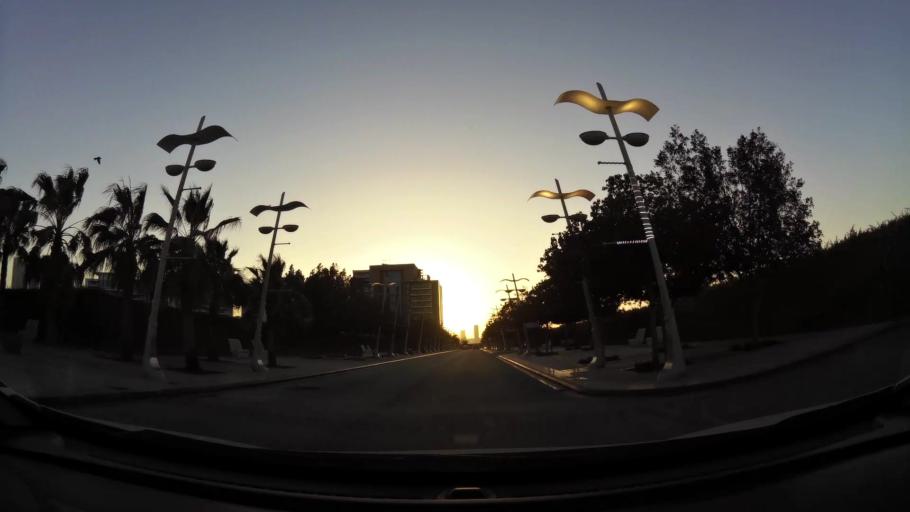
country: BH
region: Manama
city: Jidd Hafs
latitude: 26.2391
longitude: 50.5649
